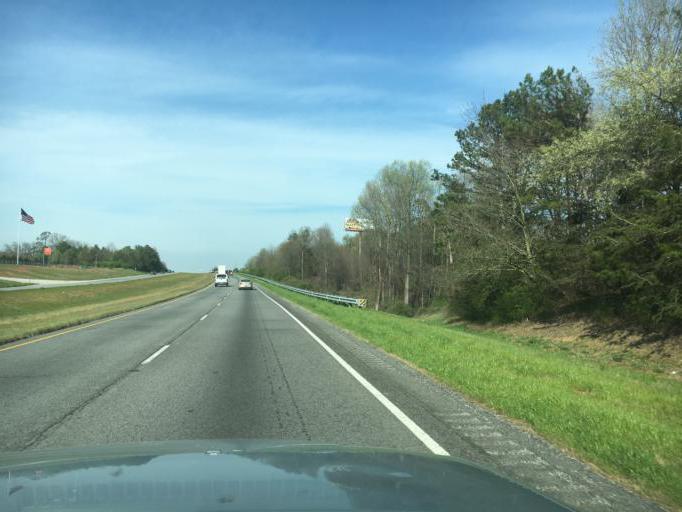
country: US
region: Georgia
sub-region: Habersham County
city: Raoul
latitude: 34.4530
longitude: -83.6131
